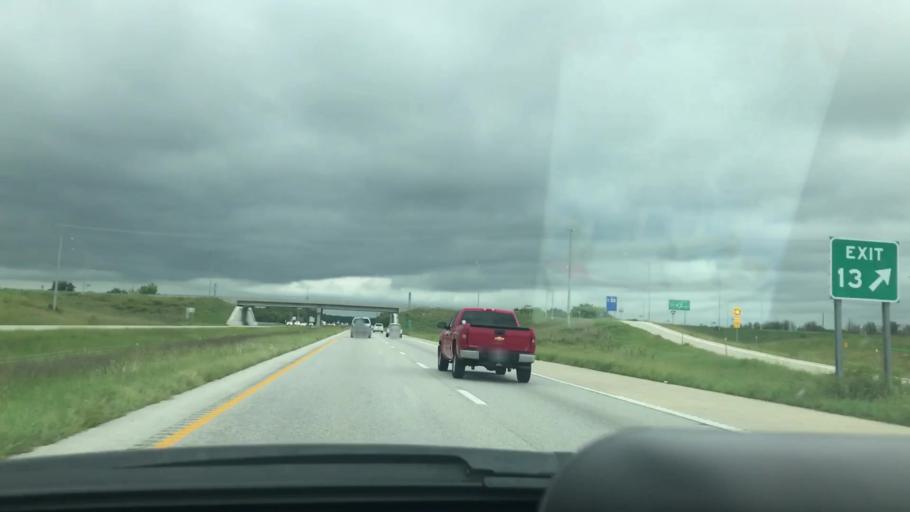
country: US
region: Missouri
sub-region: Jasper County
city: Duenweg
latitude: 37.0683
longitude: -94.4065
